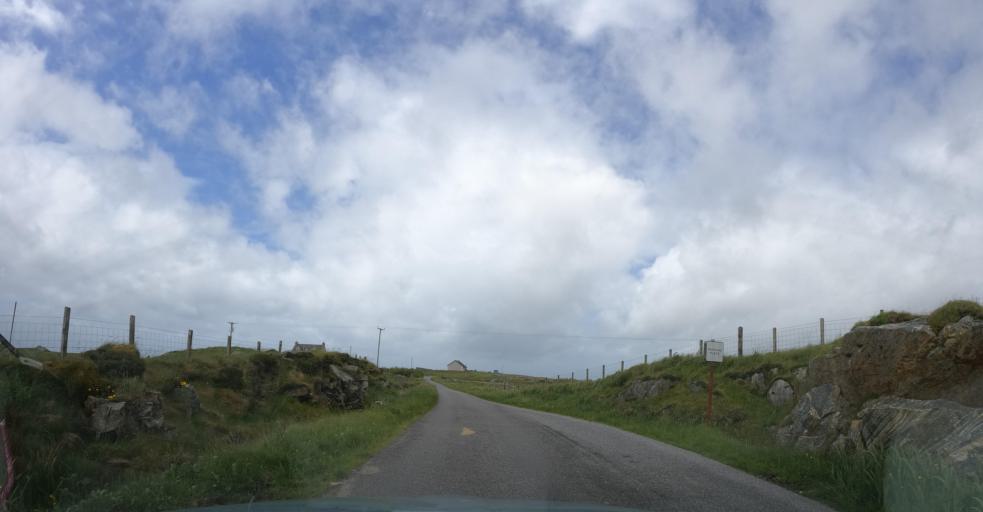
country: GB
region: Scotland
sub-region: Eilean Siar
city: Isle of South Uist
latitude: 57.2516
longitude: -7.4051
